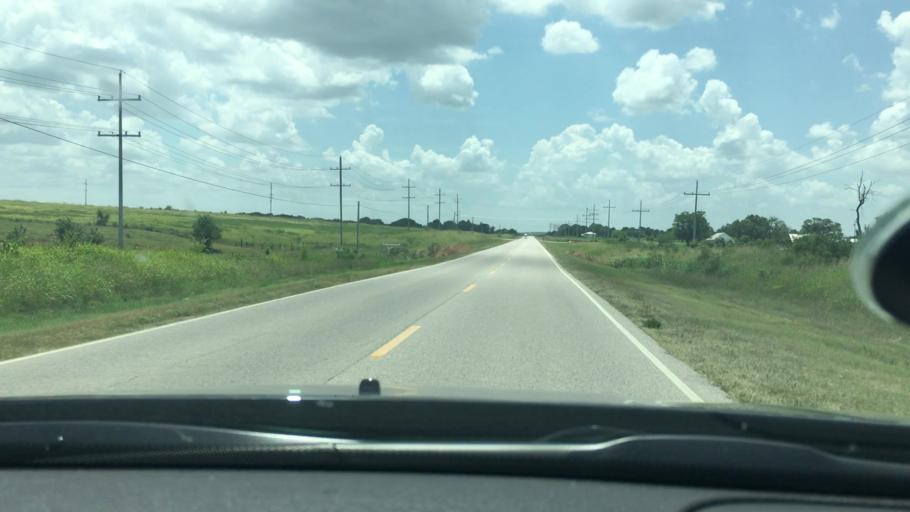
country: US
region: Oklahoma
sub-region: Pontotoc County
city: Ada
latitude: 34.6395
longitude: -96.6349
